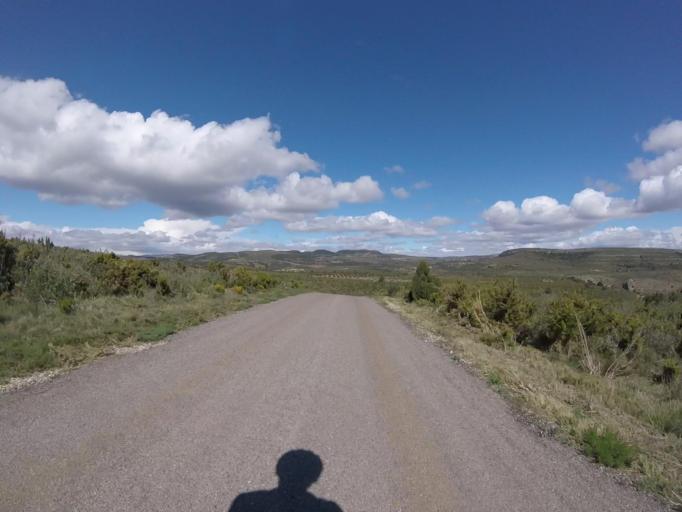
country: ES
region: Valencia
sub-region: Provincia de Castello
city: Culla
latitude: 40.3057
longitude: -0.1166
